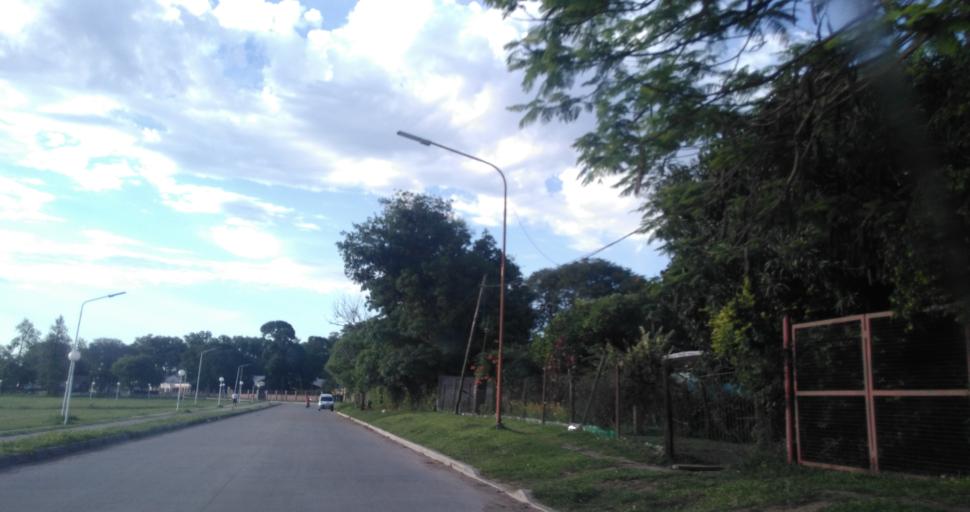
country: AR
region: Chaco
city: Fontana
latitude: -27.4188
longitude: -59.0287
